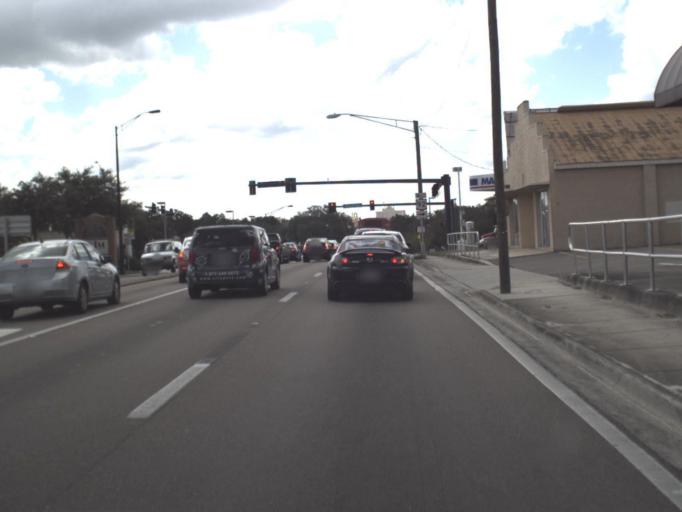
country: US
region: Florida
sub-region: Polk County
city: Lakeland
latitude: 28.0560
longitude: -81.9543
